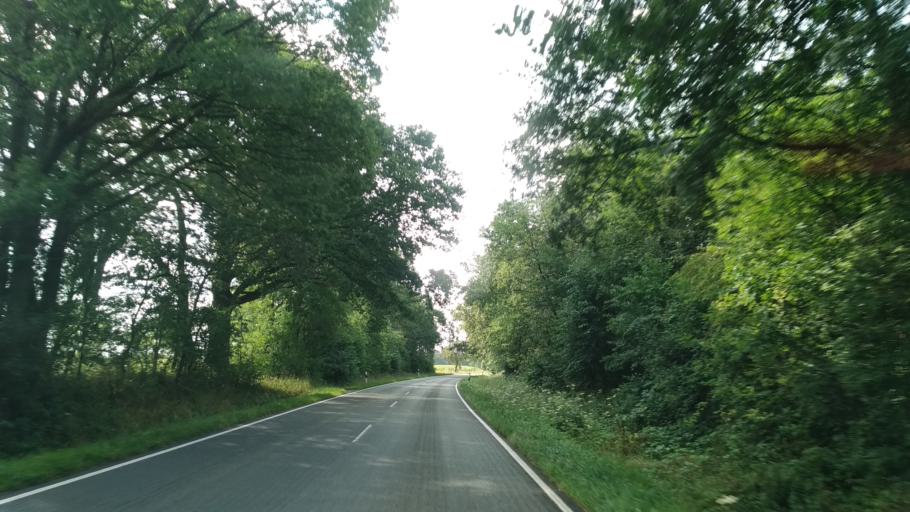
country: DE
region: Schleswig-Holstein
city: Selk
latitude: 54.4631
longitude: 9.5801
